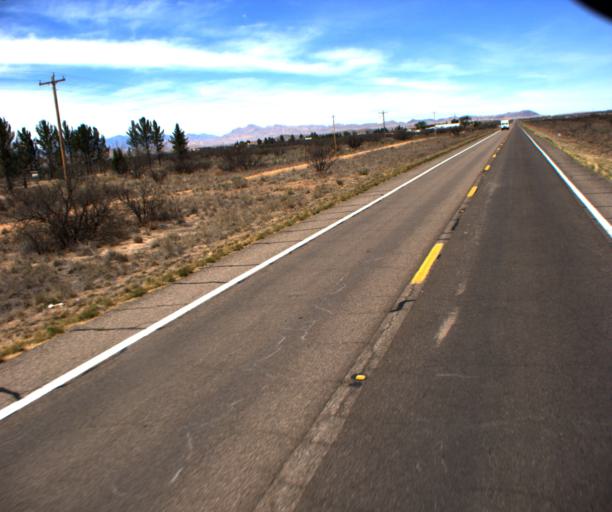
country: US
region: Arizona
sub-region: Cochise County
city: Willcox
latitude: 32.2836
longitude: -109.8110
